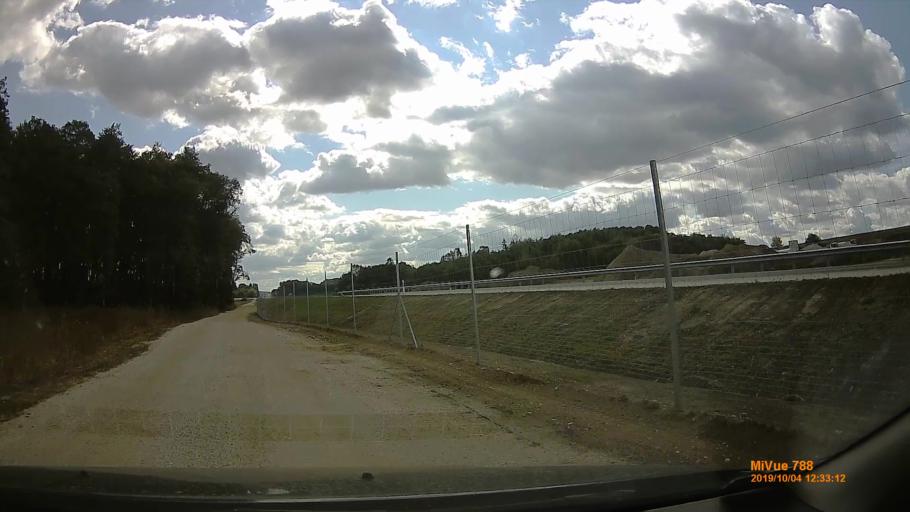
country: HU
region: Somogy
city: Karad
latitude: 46.6917
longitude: 17.7713
